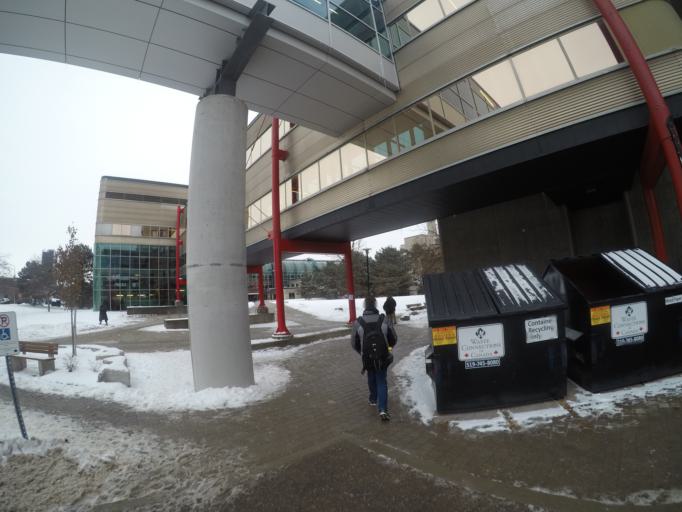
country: CA
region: Ontario
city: Waterloo
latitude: 43.4725
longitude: -80.5440
